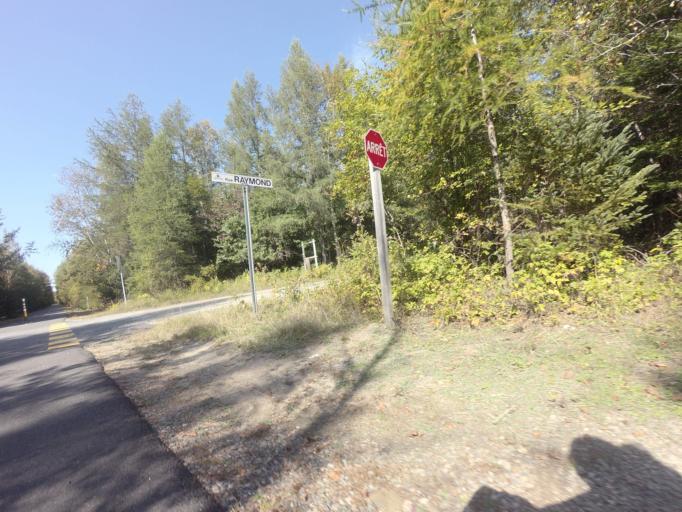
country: CA
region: Quebec
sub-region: Laurentides
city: Mont-Tremblant
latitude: 46.1228
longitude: -74.5219
